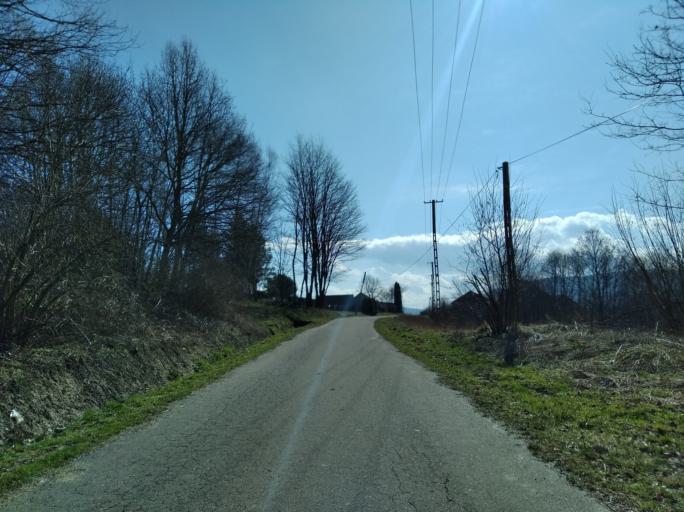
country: PL
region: Subcarpathian Voivodeship
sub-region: Powiat strzyzowski
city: Wysoka Strzyzowska
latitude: 49.8164
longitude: 21.7449
